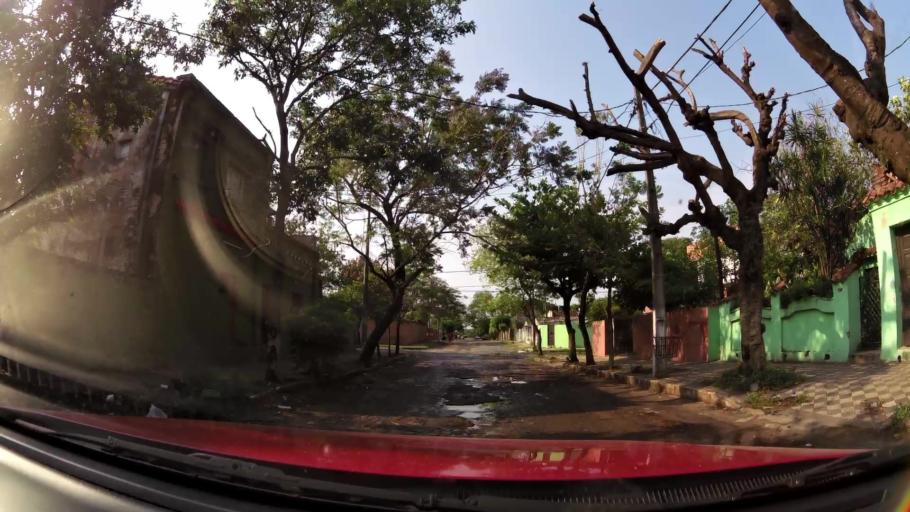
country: PY
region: Presidente Hayes
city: Nanawa
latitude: -25.2952
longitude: -57.6669
